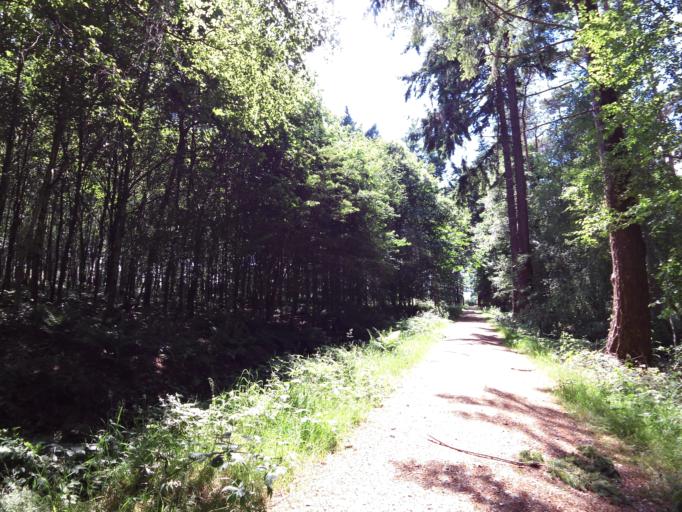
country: BE
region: Flanders
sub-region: Provincie West-Vlaanderen
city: Zedelgem
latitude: 51.1416
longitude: 3.1049
